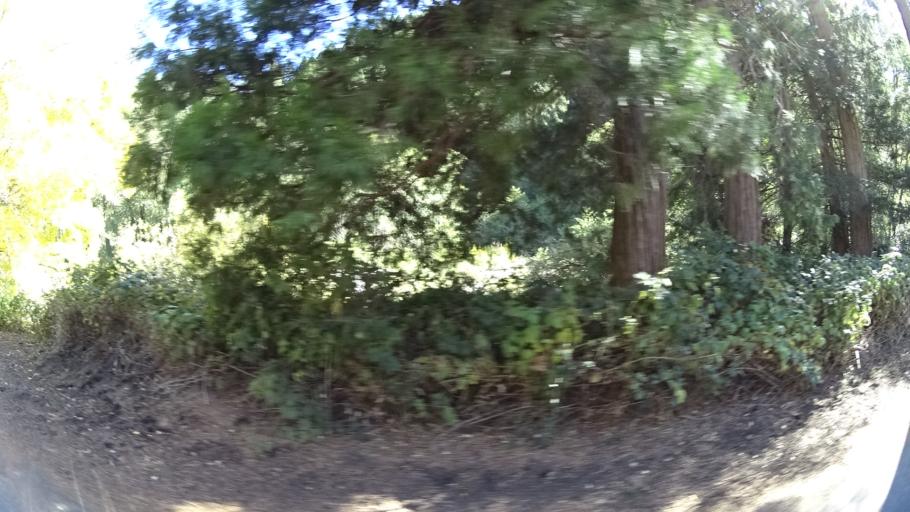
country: US
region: California
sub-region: Siskiyou County
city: Happy Camp
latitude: 41.2983
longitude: -123.1254
